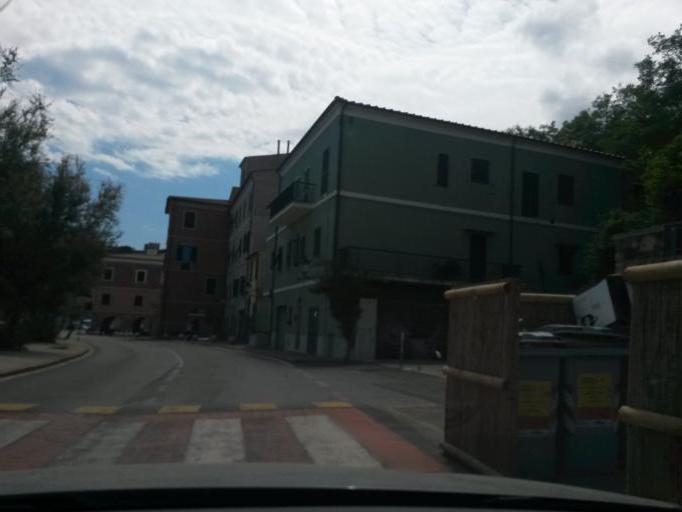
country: IT
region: Tuscany
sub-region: Provincia di Livorno
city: Rio Marina
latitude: 42.8177
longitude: 10.4289
